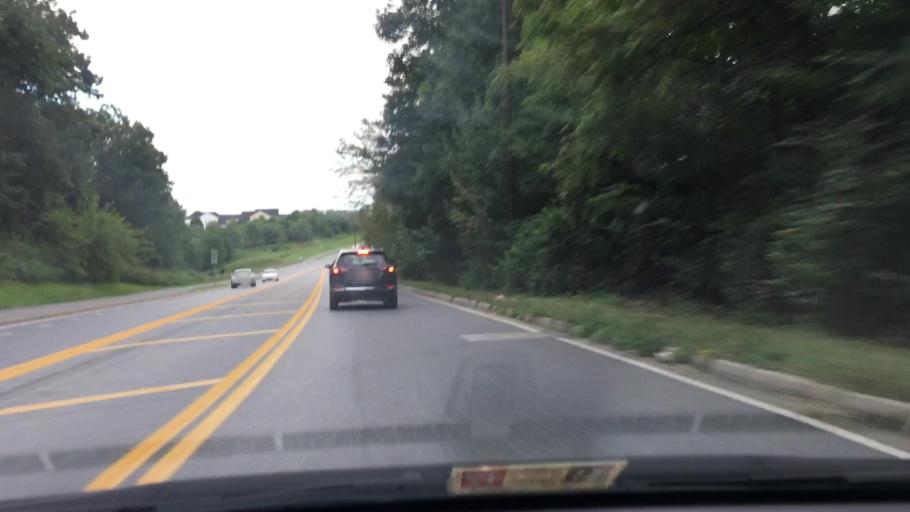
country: US
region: Maryland
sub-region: Prince George's County
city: West Laurel
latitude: 39.0931
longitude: -76.8760
